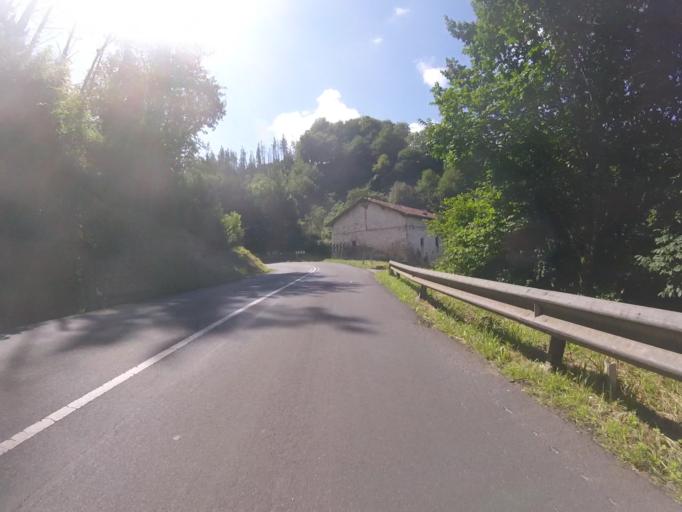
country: ES
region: Basque Country
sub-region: Provincia de Guipuzcoa
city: Errezil
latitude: 43.1749
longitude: -2.2136
